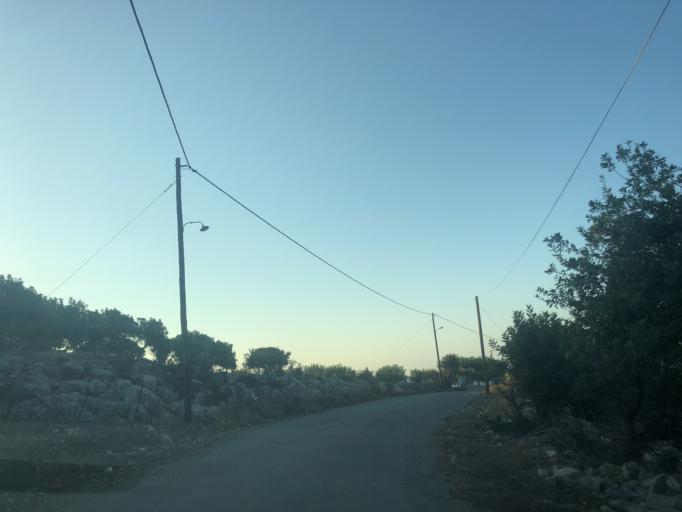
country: GR
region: Crete
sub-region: Nomos Rethymnis
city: Atsipopoulon
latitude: 35.3566
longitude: 24.3971
